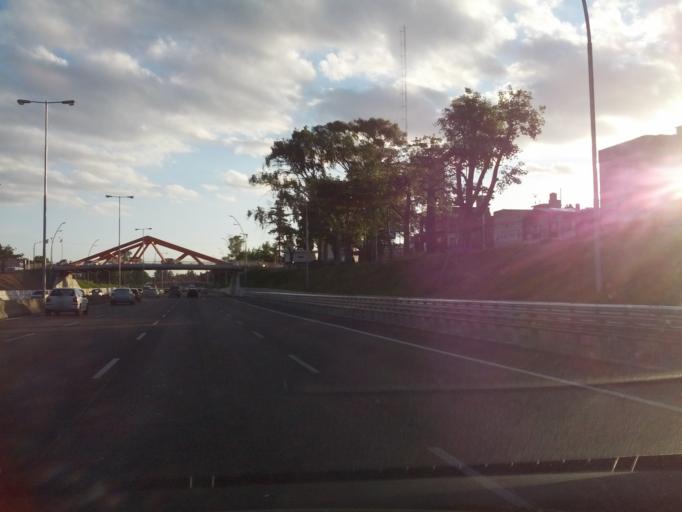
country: AR
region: Buenos Aires
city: Caseros
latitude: -34.6100
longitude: -58.5284
